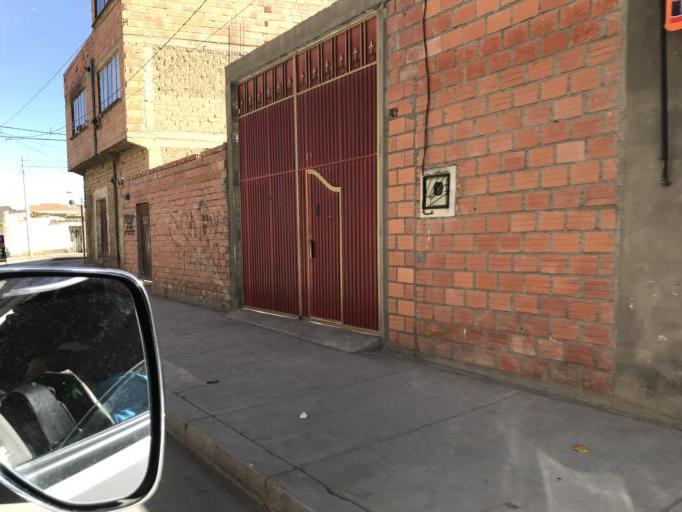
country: BO
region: La Paz
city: La Paz
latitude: -16.4868
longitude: -68.1823
